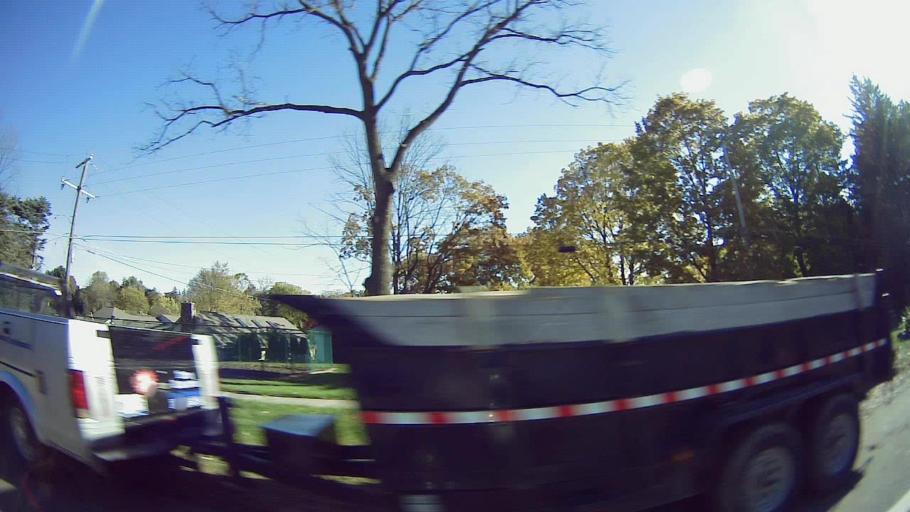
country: US
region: Michigan
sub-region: Oakland County
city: Farmington
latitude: 42.4736
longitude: -83.3768
